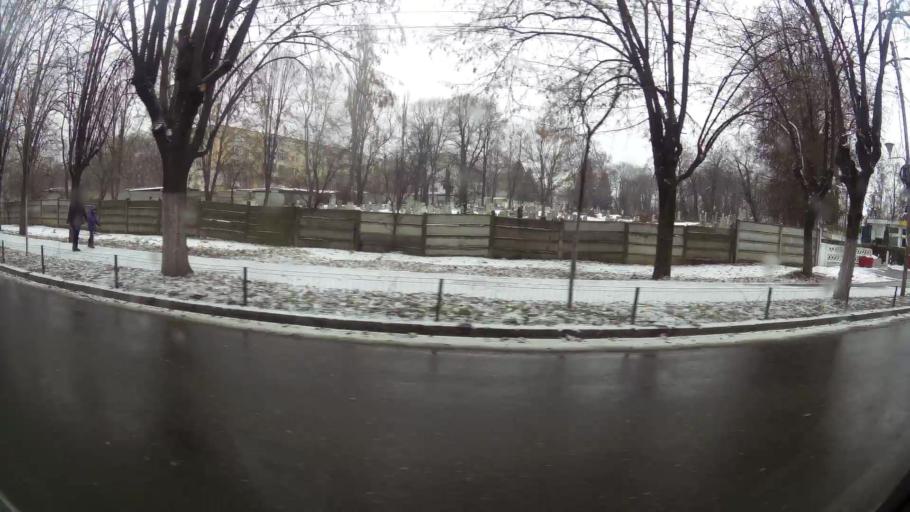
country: RO
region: Prahova
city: Ploiesti
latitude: 44.9561
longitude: 26.0083
